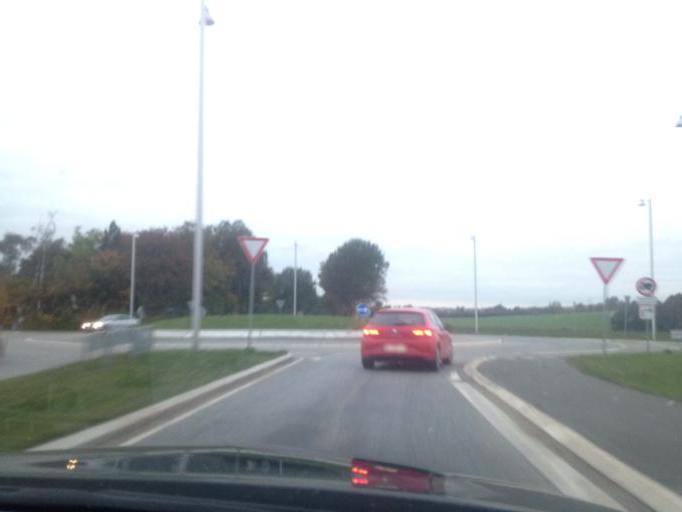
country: DK
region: Zealand
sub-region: Solrod Kommune
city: Havdrup
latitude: 55.5649
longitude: 12.1277
